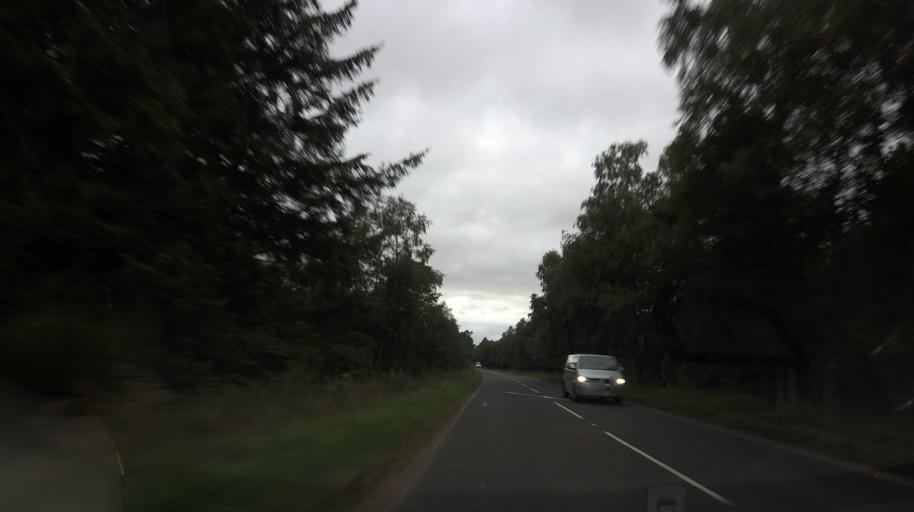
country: GB
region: Scotland
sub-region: Aberdeenshire
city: Torphins
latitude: 57.2031
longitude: -2.5992
